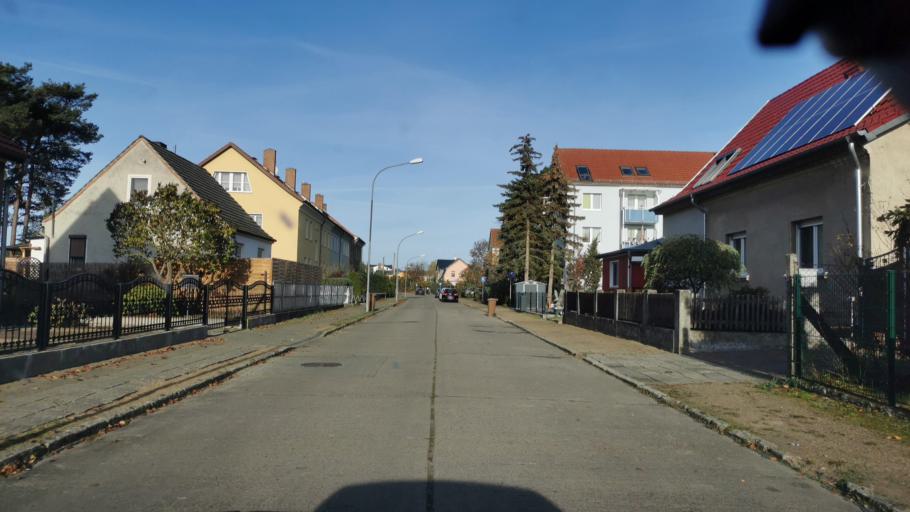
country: DE
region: Brandenburg
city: Britz
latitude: 52.8727
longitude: 13.8250
